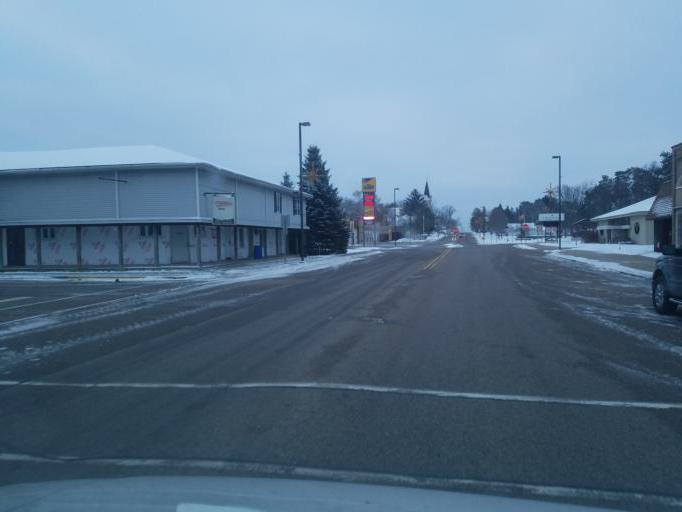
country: US
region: Wisconsin
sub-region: Waupaca County
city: Manawa
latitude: 44.4634
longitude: -88.9200
